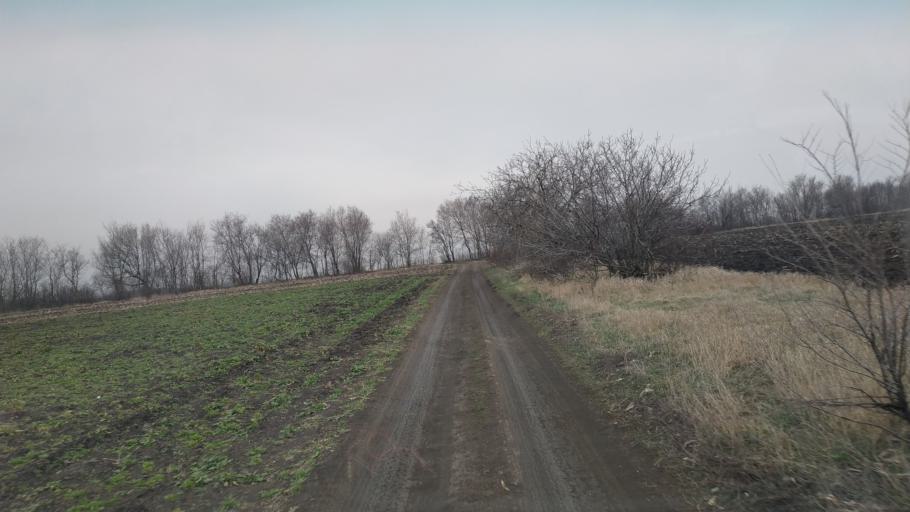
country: MD
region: Chisinau
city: Singera
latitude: 46.8290
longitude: 28.9944
